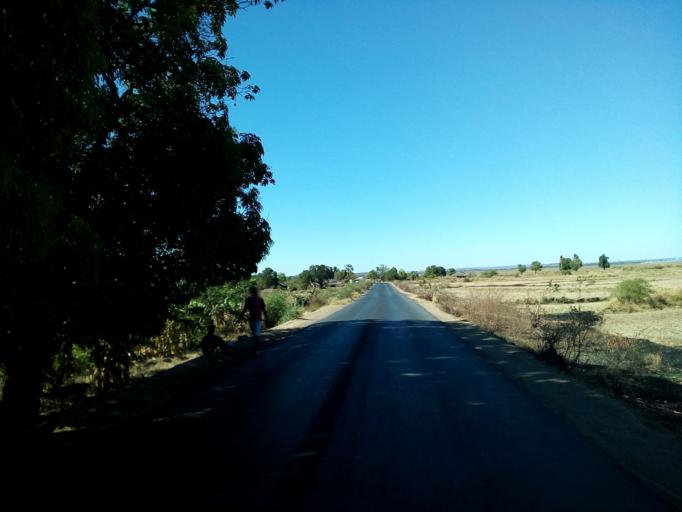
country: MG
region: Boeny
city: Marovoay
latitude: -16.0875
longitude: 46.7444
